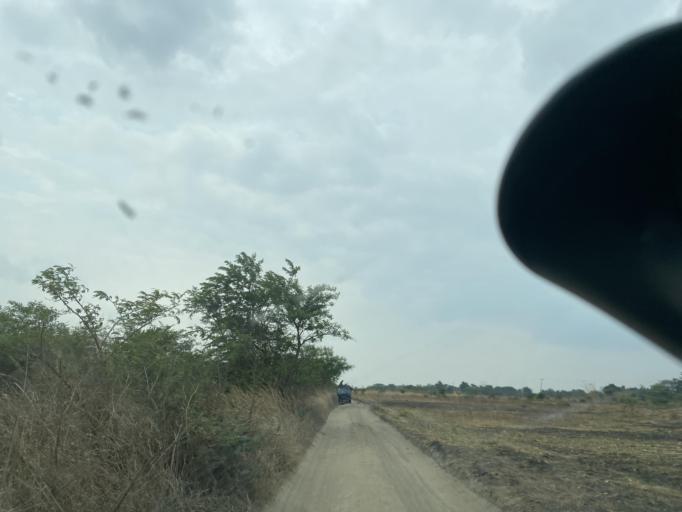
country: ZM
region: Lusaka
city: Lusaka
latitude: -15.2482
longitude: 28.3320
